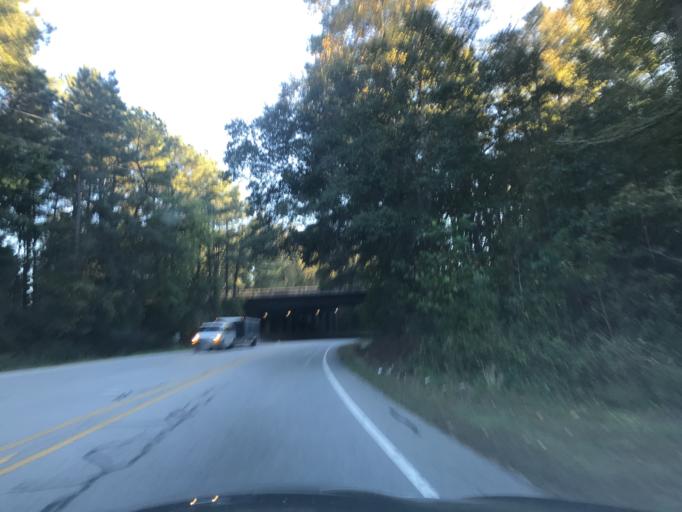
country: US
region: North Carolina
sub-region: Wake County
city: Garner
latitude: 35.7552
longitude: -78.5825
